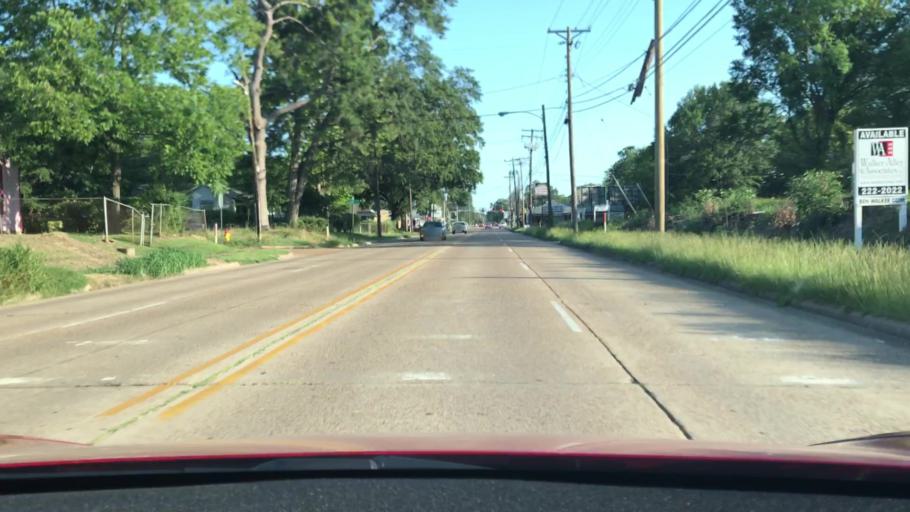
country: US
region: Louisiana
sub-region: Bossier Parish
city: Bossier City
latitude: 32.4450
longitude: -93.7460
